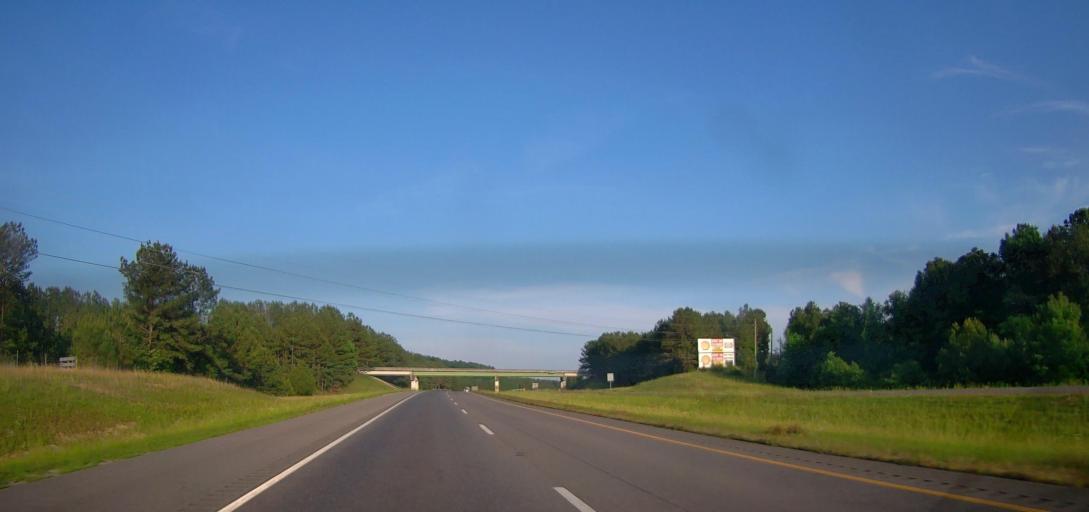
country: US
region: Alabama
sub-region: Marion County
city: Hamilton
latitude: 34.1154
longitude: -88.0332
